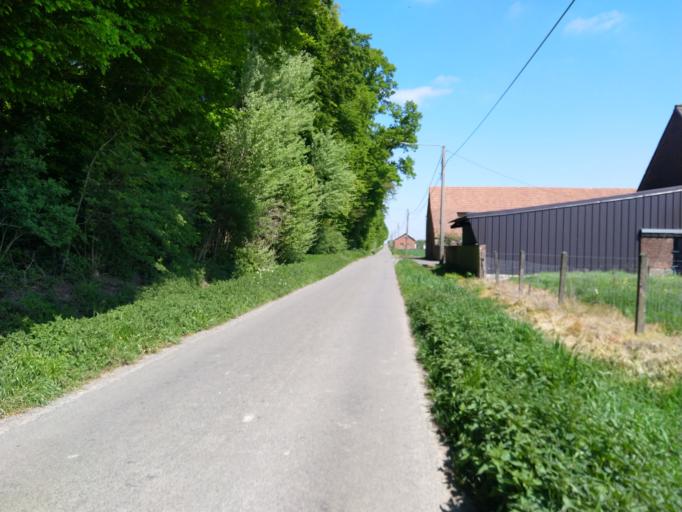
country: BE
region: Wallonia
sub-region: Province du Hainaut
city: Brugelette
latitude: 50.5485
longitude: 3.8468
